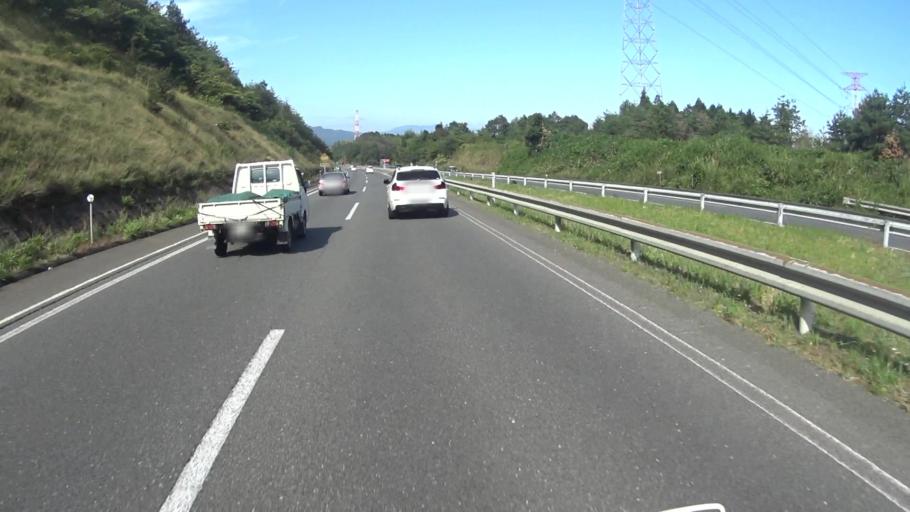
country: JP
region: Kyoto
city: Kameoka
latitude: 34.9895
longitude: 135.6300
